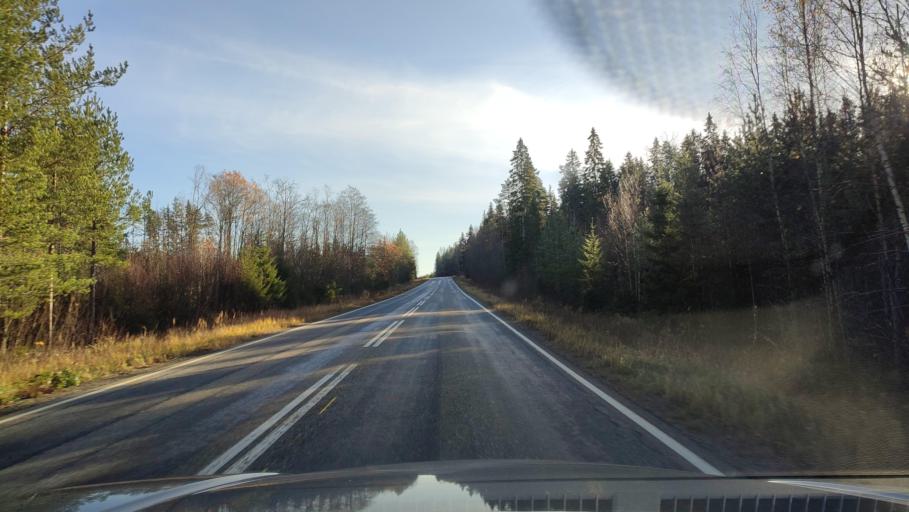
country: FI
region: Southern Ostrobothnia
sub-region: Suupohja
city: Karijoki
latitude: 62.2362
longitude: 21.6971
